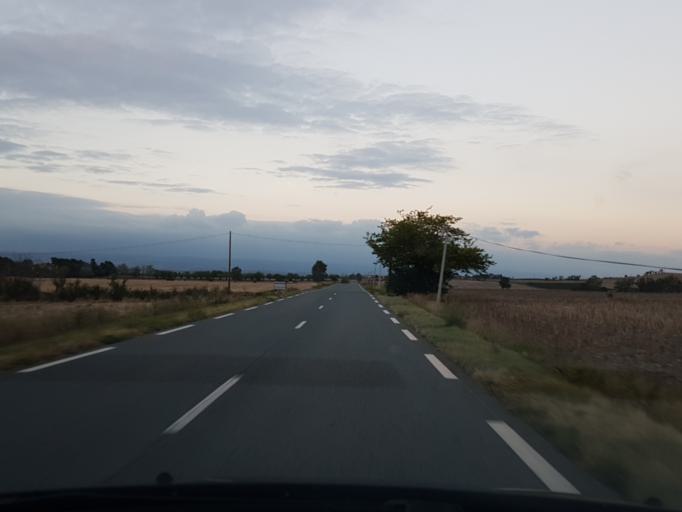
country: FR
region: Languedoc-Roussillon
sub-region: Departement de l'Aude
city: Bram
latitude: 43.2138
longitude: 2.0732
